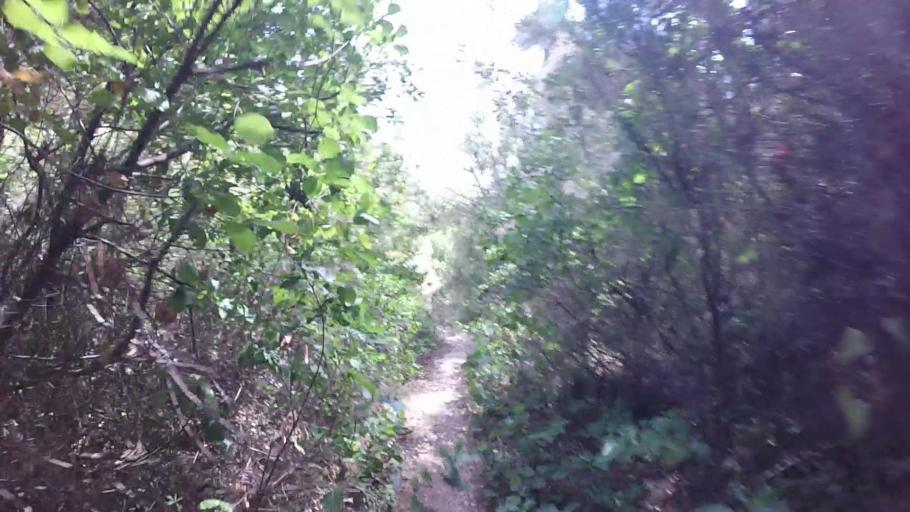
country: FR
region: Provence-Alpes-Cote d'Azur
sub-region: Departement des Alpes-Maritimes
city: Mougins
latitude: 43.6192
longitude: 7.0305
